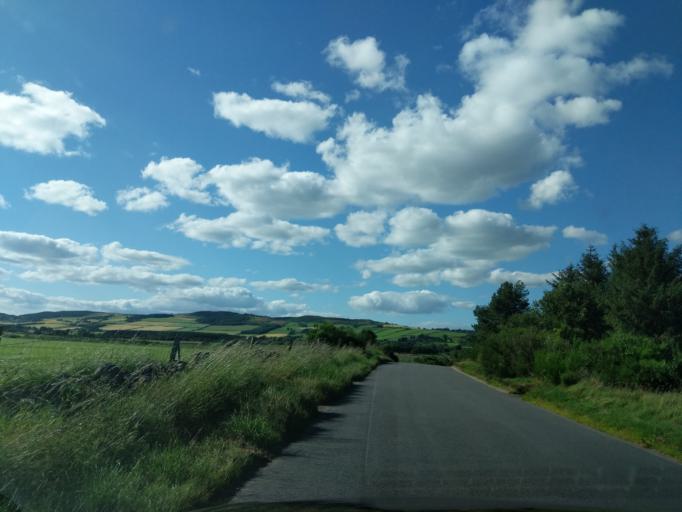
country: GB
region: Scotland
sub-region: Aberdeenshire
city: Torphins
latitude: 57.0118
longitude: -2.5851
